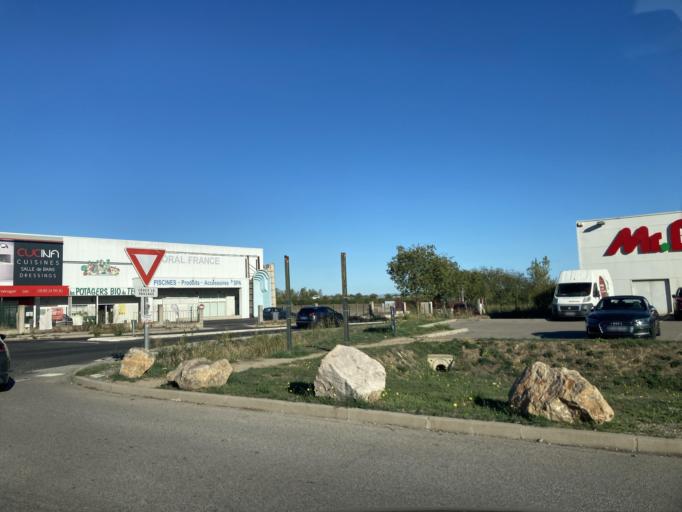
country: FR
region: Languedoc-Roussillon
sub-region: Departement des Pyrenees-Orientales
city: Sant Genis de Fontanes
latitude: 42.5476
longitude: 2.9424
